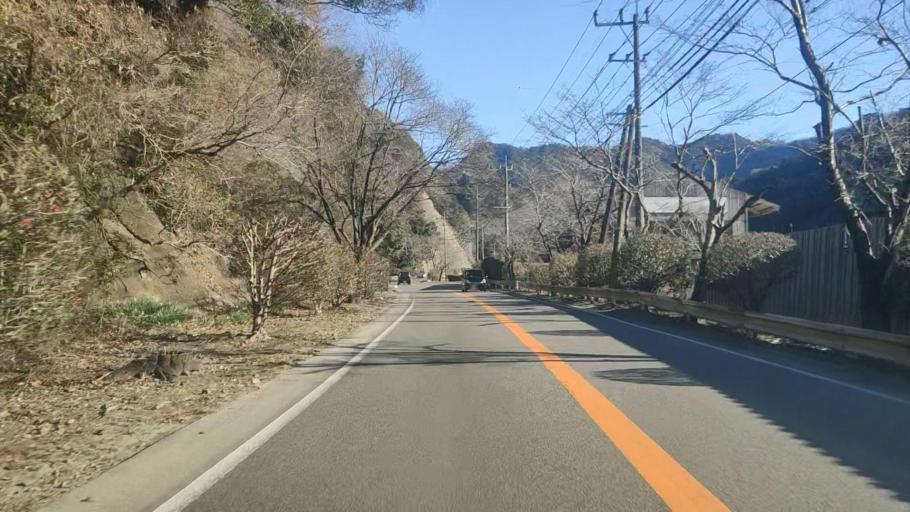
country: JP
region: Miyazaki
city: Nobeoka
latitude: 32.6222
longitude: 131.7082
